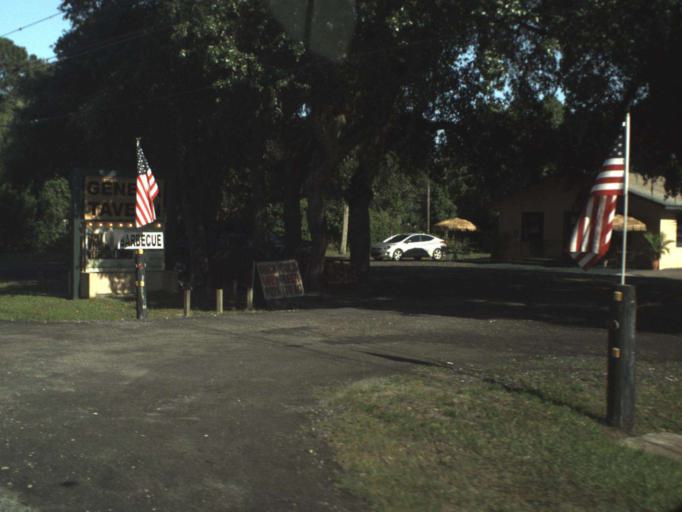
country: US
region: Florida
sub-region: Seminole County
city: Geneva
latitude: 28.7172
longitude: -81.0622
